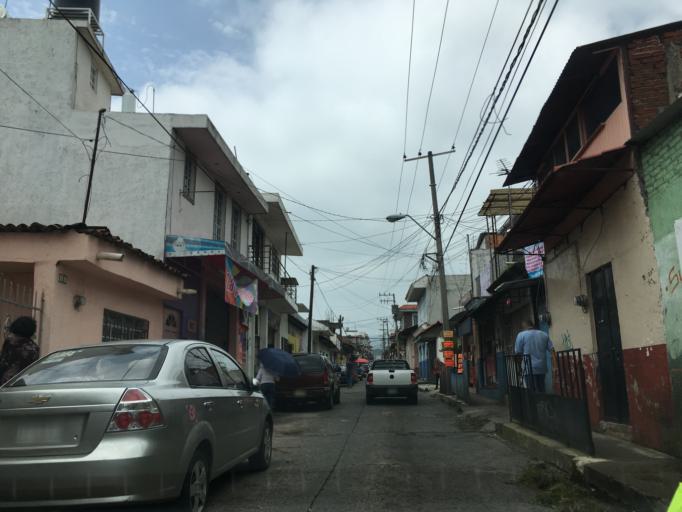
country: MX
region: Michoacan
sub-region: Uruapan
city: Uruapan
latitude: 19.4217
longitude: -102.0583
